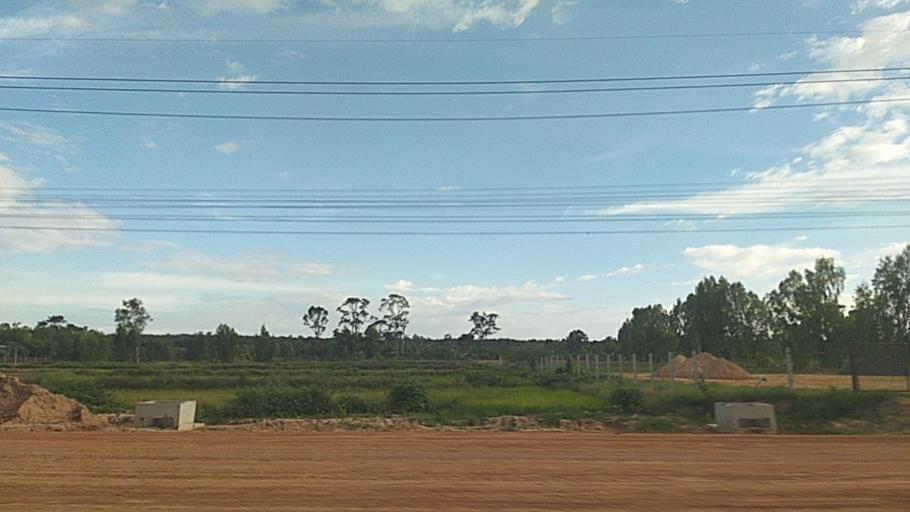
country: TH
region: Surin
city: Kap Choeng
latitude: 14.4567
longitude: 103.6755
